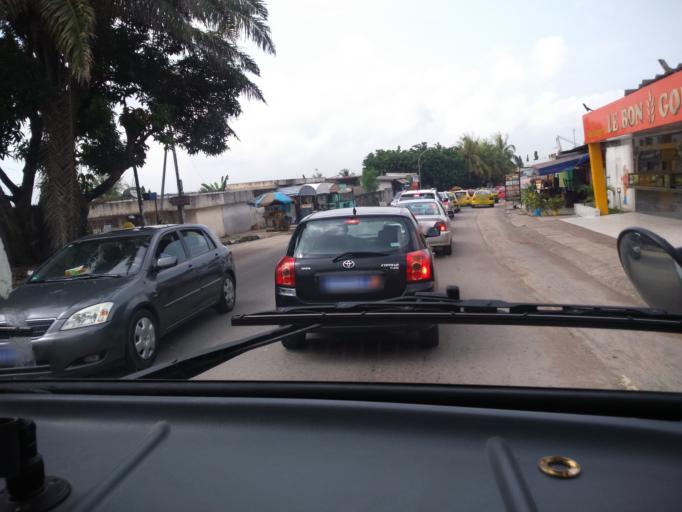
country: CI
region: Lagunes
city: Abobo
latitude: 5.3688
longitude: -3.9801
